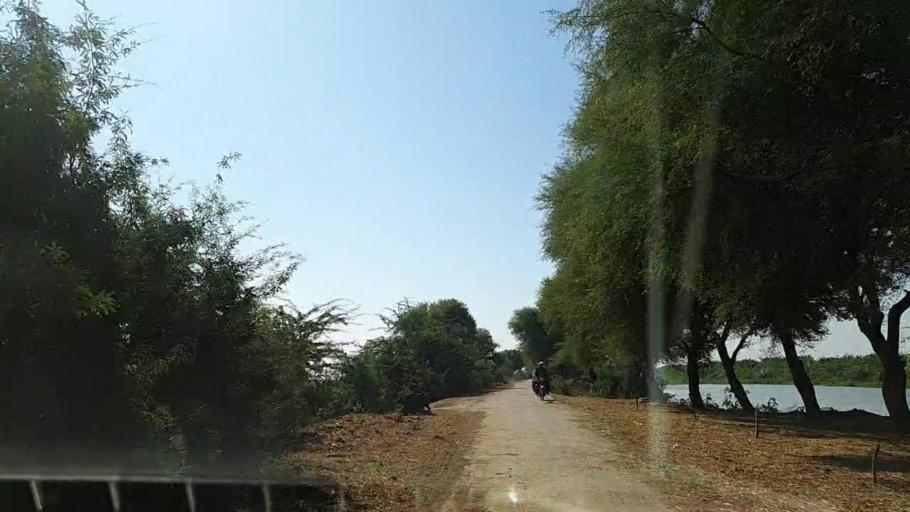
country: PK
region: Sindh
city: Chuhar Jamali
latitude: 24.5840
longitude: 68.0477
